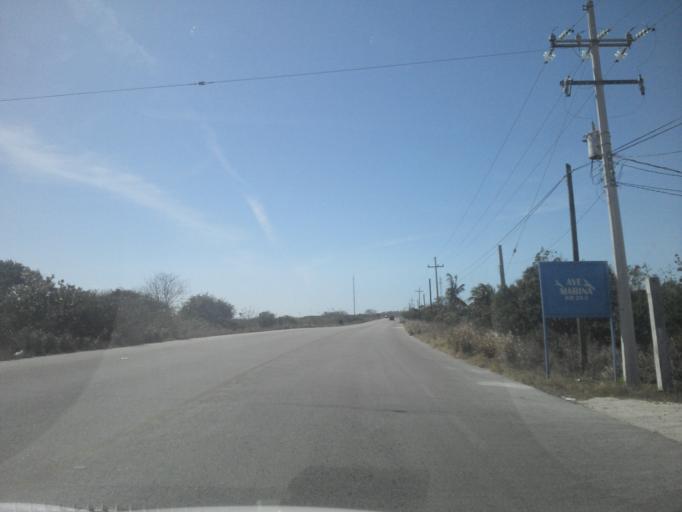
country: MX
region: Yucatan
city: Telchac Puerto
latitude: 21.3290
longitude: -89.3850
